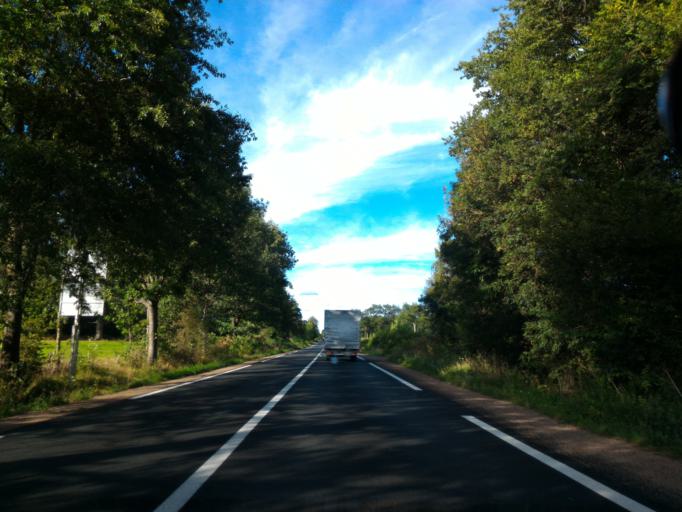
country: FR
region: Limousin
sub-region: Departement de la Haute-Vienne
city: Magnac-Laval
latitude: 46.1697
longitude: 1.1465
